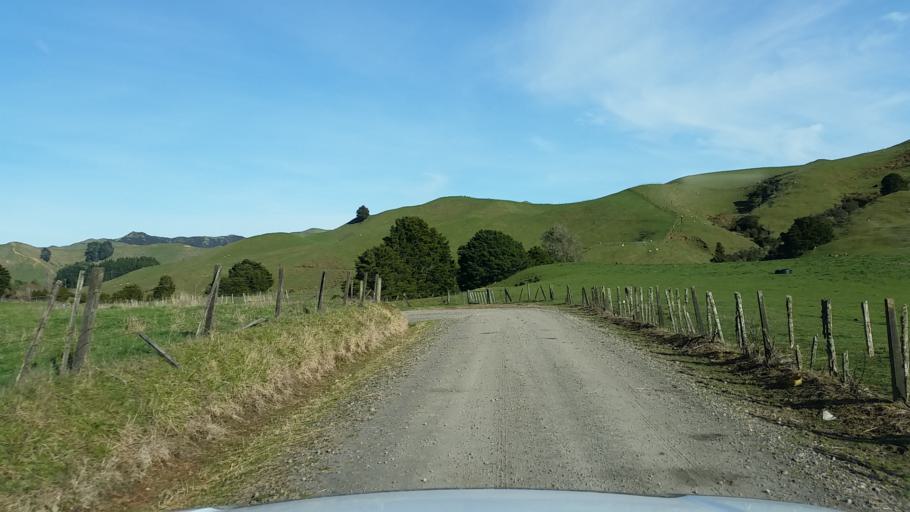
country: NZ
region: Taranaki
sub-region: South Taranaki District
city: Eltham
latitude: -39.3127
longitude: 174.5364
